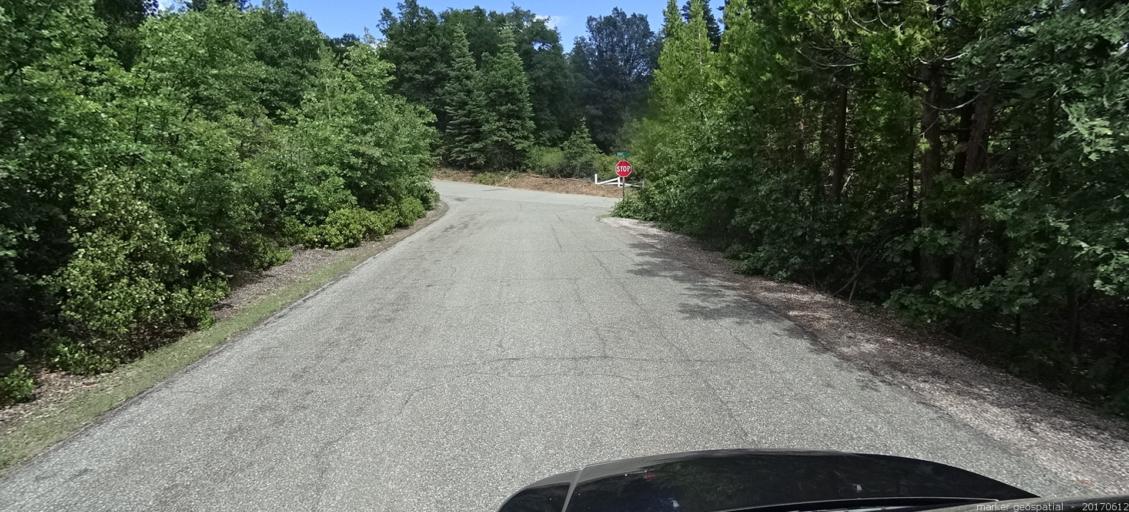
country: US
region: California
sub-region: Siskiyou County
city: Mount Shasta
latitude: 41.3037
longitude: -122.2985
